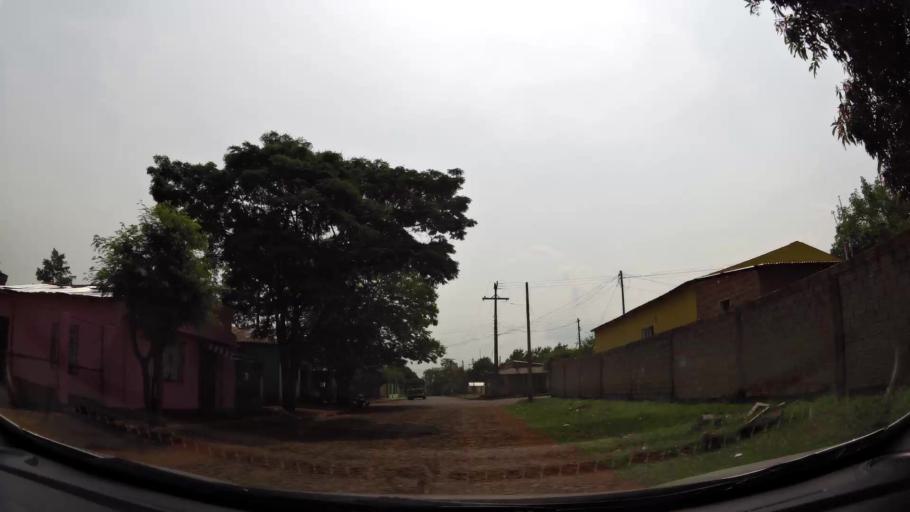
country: BR
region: Parana
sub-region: Foz Do Iguacu
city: Foz do Iguacu
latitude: -25.5717
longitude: -54.6120
